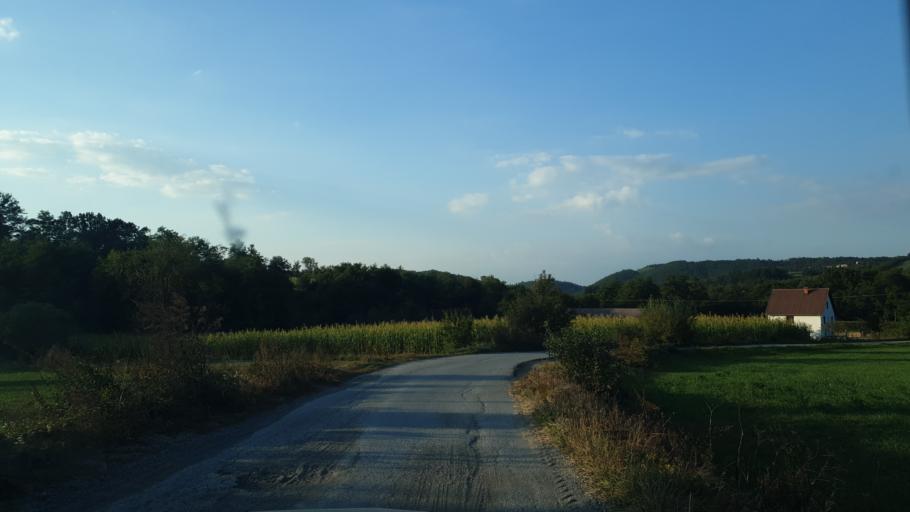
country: RS
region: Central Serbia
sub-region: Zlatiborski Okrug
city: Kosjeric
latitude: 43.9717
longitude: 20.0229
